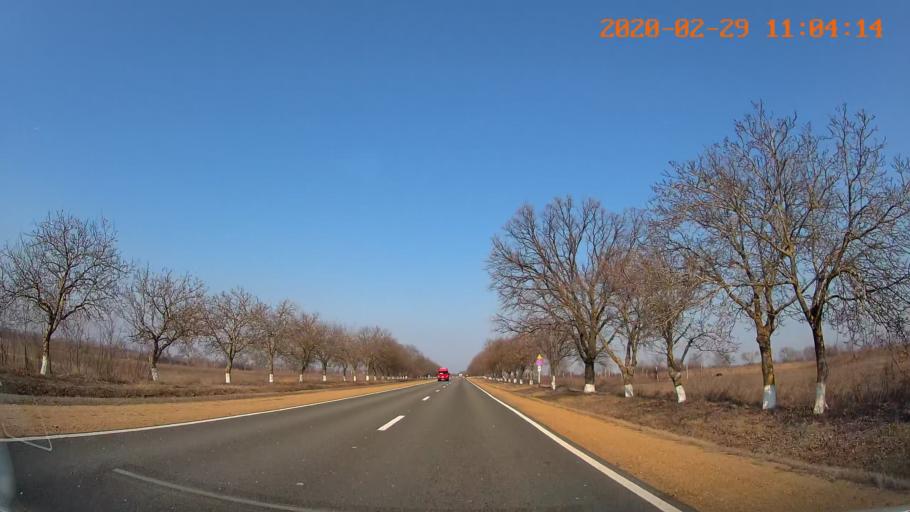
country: MD
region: Criuleni
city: Criuleni
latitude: 47.1864
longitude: 29.2048
